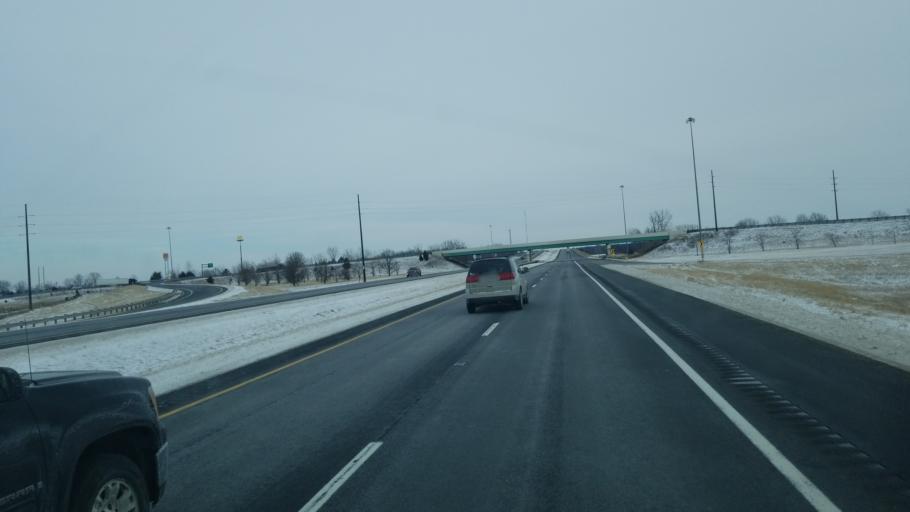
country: US
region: Ohio
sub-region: Wyandot County
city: Carey
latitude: 40.9416
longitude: -83.4031
